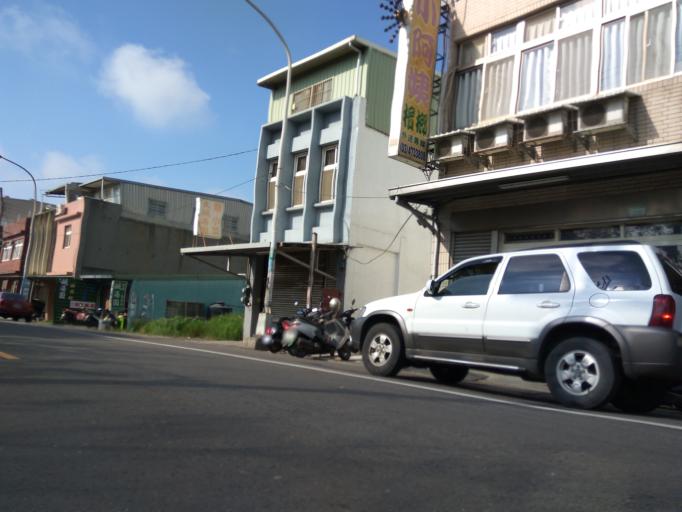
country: TW
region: Taiwan
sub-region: Hsinchu
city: Zhubei
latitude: 25.0346
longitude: 121.0872
